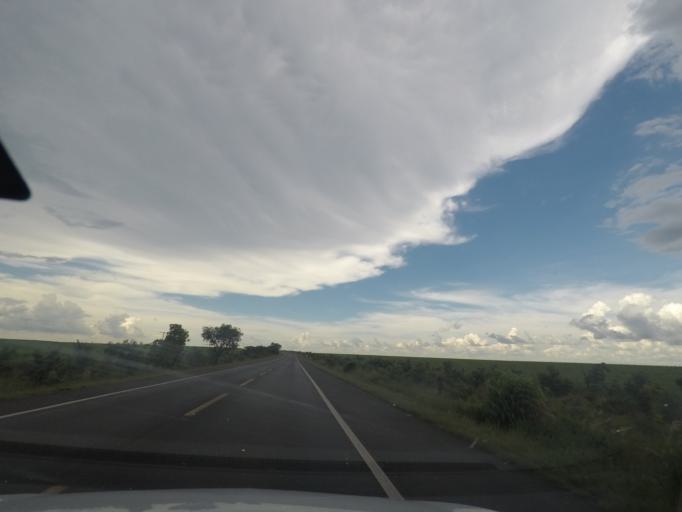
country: BR
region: Minas Gerais
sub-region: Prata
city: Prata
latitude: -19.6235
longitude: -48.8451
